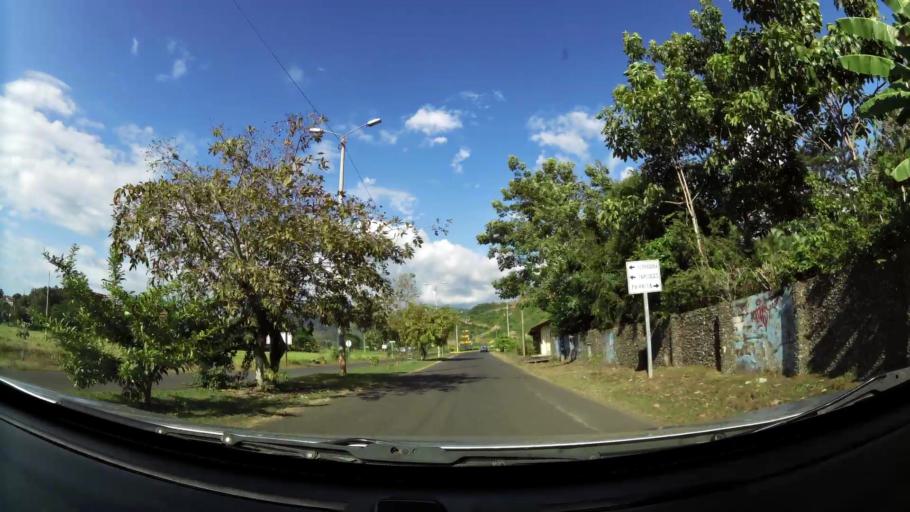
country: CR
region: Puntarenas
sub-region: Canton de Garabito
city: Jaco
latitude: 9.6345
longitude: -84.6282
